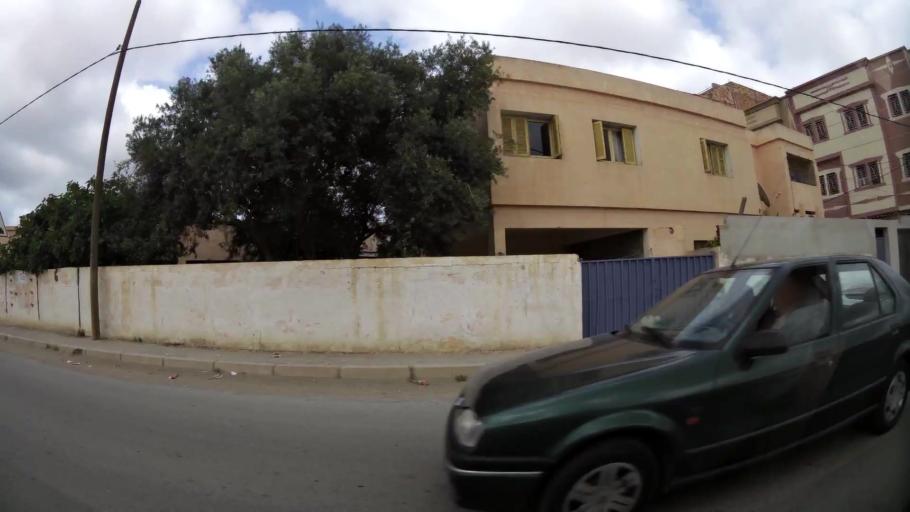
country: MA
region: Oriental
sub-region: Nador
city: Nador
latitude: 35.1639
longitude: -2.9410
